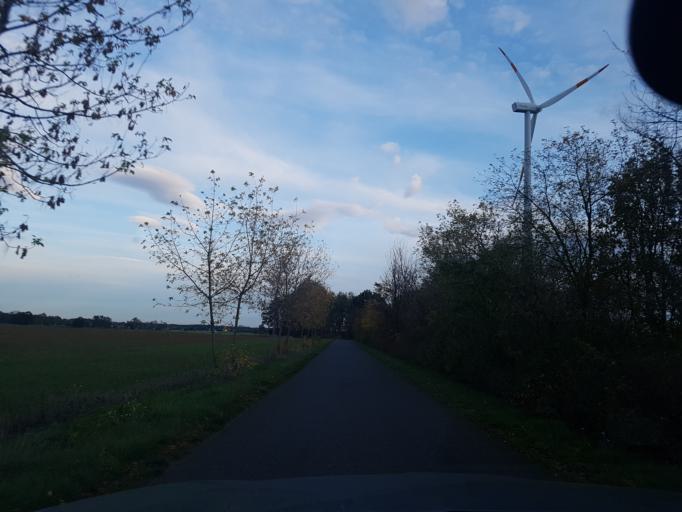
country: DE
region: Brandenburg
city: Elsterwerda
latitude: 51.4527
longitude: 13.4815
